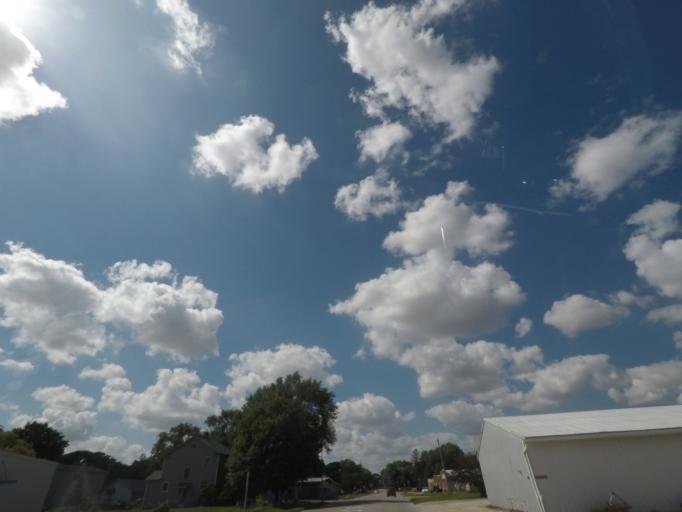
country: US
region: Iowa
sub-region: Story County
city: Nevada
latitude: 42.0228
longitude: -93.4415
